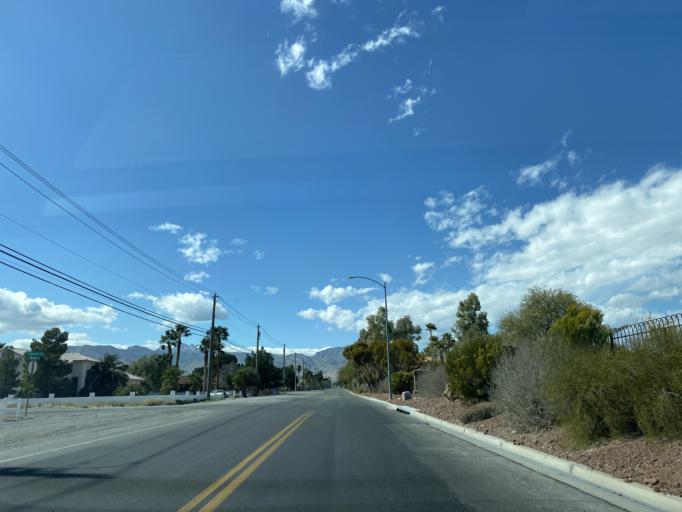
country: US
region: Nevada
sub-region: Clark County
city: Spring Valley
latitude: 36.2556
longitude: -115.2691
